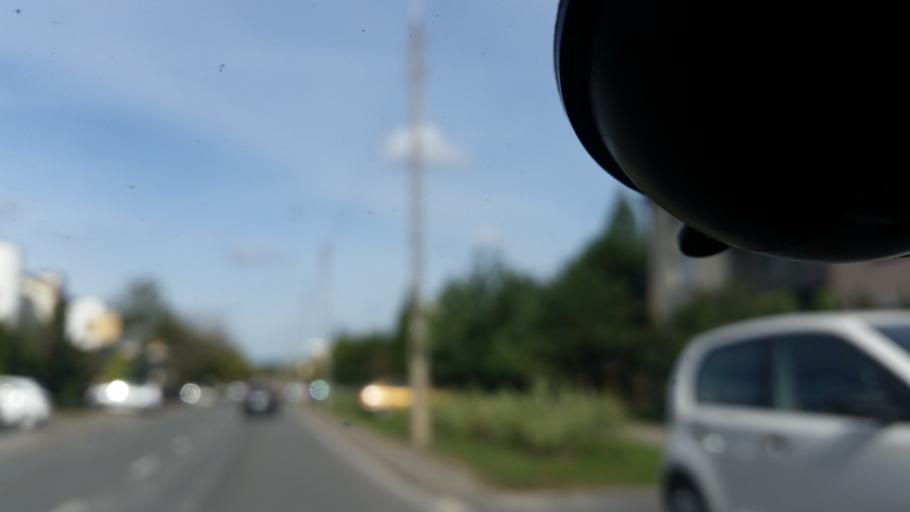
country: PL
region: Masovian Voivodeship
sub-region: Warszawa
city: Zoliborz
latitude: 52.2795
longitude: 20.9679
